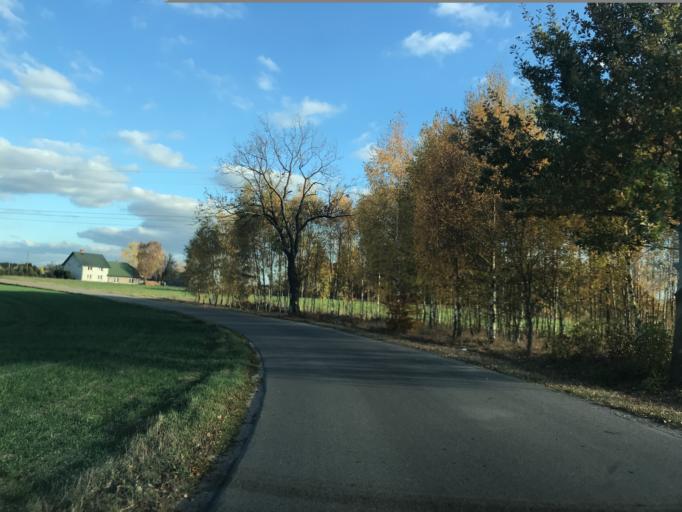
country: PL
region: Warmian-Masurian Voivodeship
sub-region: Powiat dzialdowski
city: Rybno
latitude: 53.3768
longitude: 19.8235
